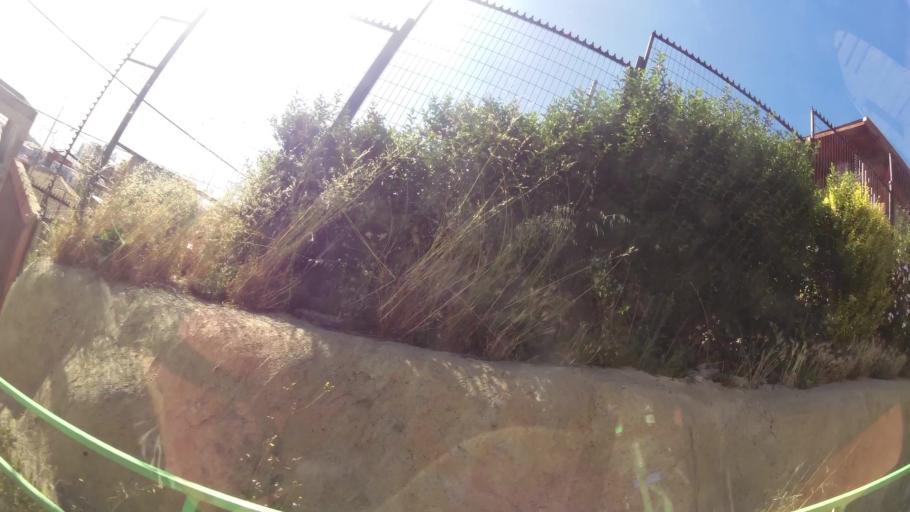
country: CL
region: Valparaiso
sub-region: Provincia de Valparaiso
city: Valparaiso
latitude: -33.0513
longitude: -71.6381
